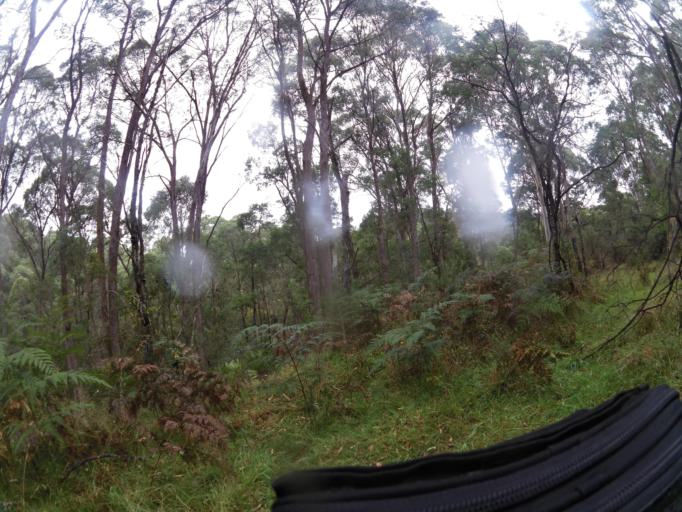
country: AU
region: New South Wales
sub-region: Greater Hume Shire
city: Holbrook
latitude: -36.2316
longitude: 147.6021
